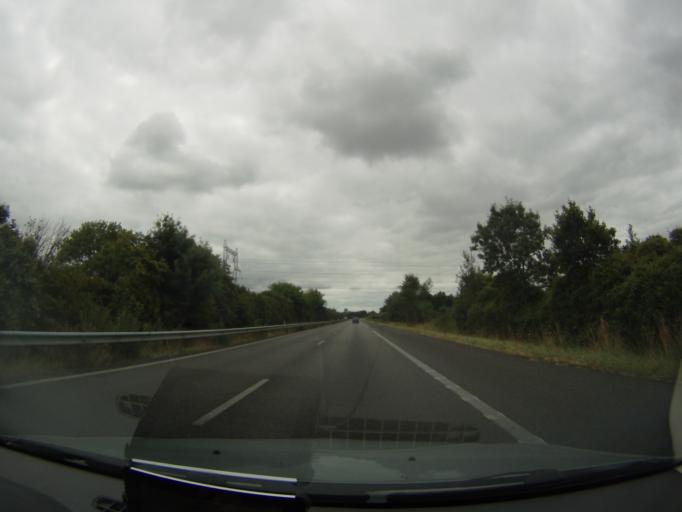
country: FR
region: Pays de la Loire
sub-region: Departement de la Loire-Atlantique
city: Heric
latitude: 47.4268
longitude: -1.6378
